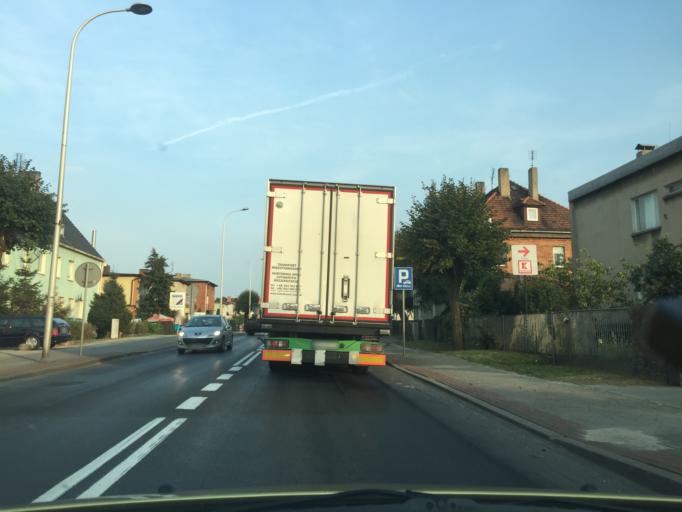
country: PL
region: Greater Poland Voivodeship
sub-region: Powiat jarocinski
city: Jarocin
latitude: 51.9754
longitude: 17.4955
